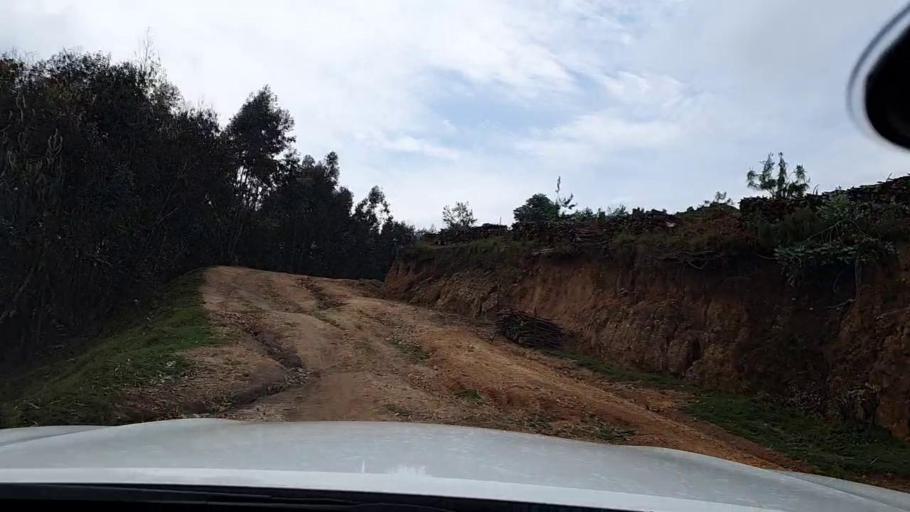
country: RW
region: Western Province
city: Kibuye
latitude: -2.2010
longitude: 29.3209
